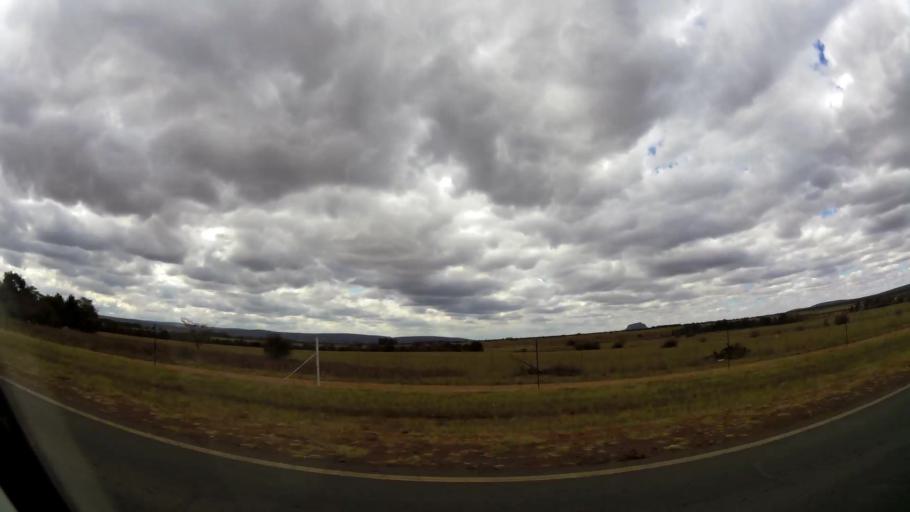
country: ZA
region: Limpopo
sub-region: Waterberg District Municipality
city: Modimolle
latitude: -24.7422
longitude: 28.4390
